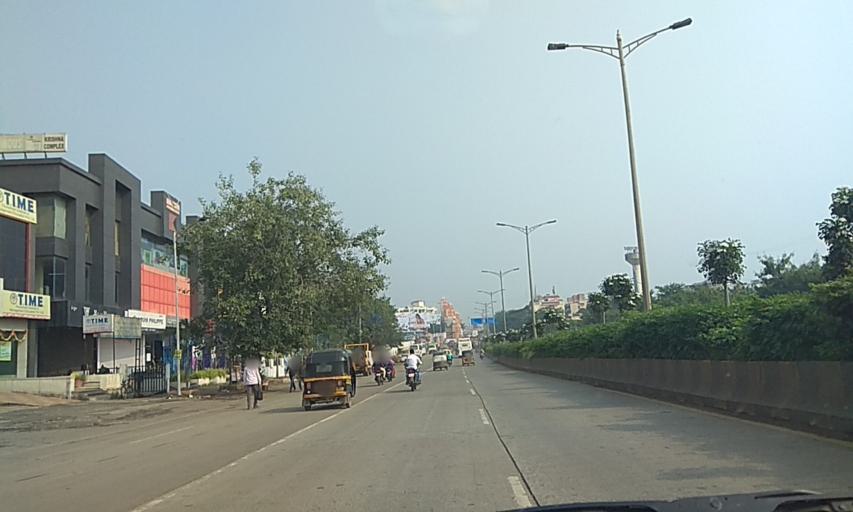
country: IN
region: Maharashtra
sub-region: Pune Division
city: Lohogaon
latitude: 18.5559
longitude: 73.9377
